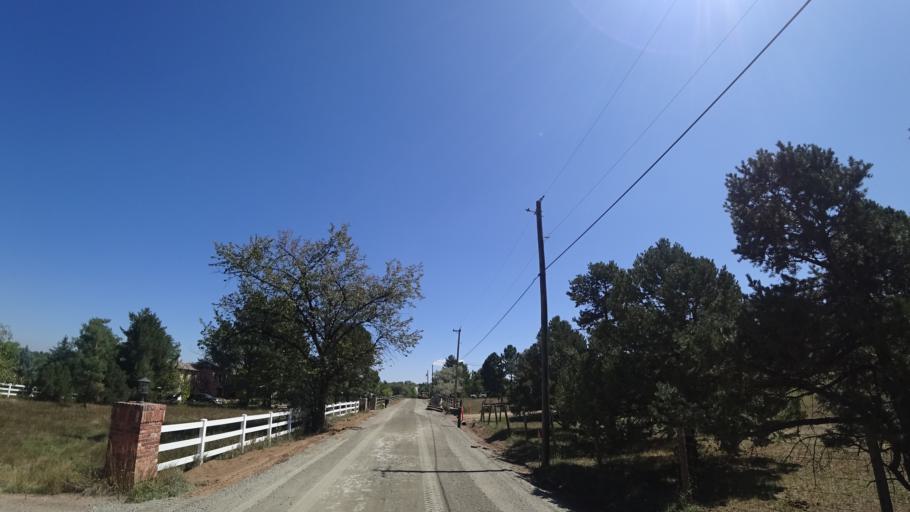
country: US
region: Colorado
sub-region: Arapahoe County
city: Greenwood Village
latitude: 39.6168
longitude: -104.9577
